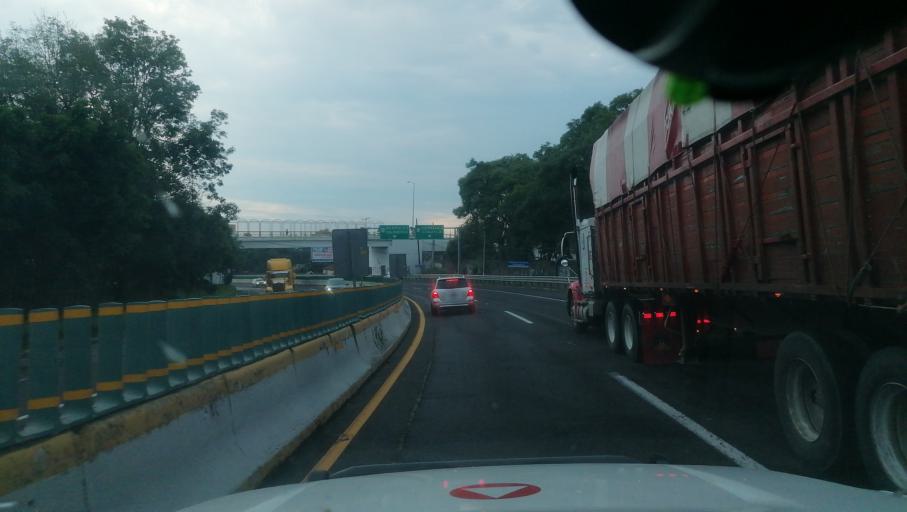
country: MX
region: Morelos
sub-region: Cuernavaca
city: Fraccionamiento Lomas de Ahuatlan
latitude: 18.9736
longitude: -99.2389
